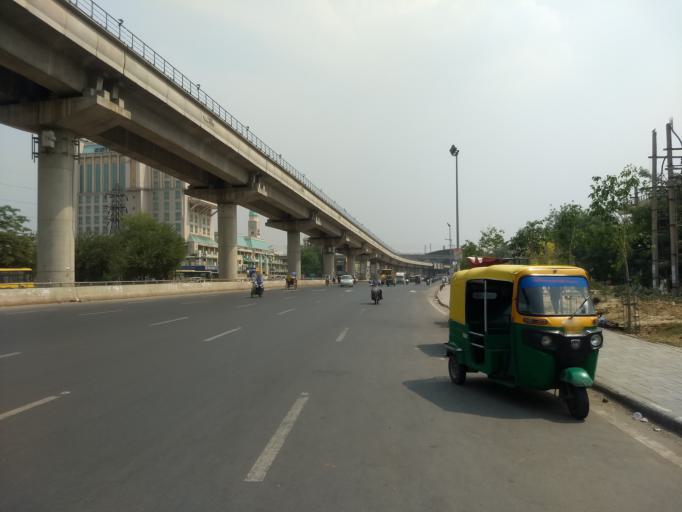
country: IN
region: Haryana
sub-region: Gurgaon
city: Gurgaon
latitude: 28.4846
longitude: 77.0949
